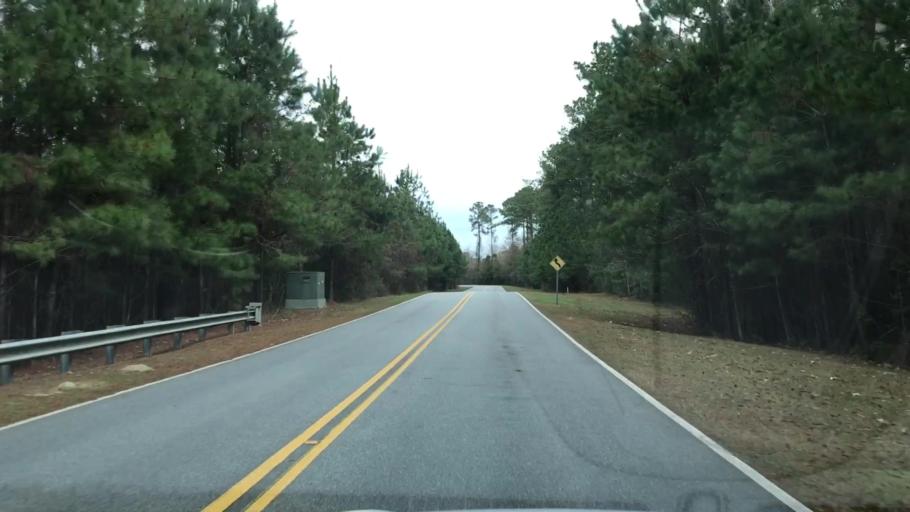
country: US
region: South Carolina
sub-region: Beaufort County
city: Bluffton
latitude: 32.2817
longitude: -80.9274
